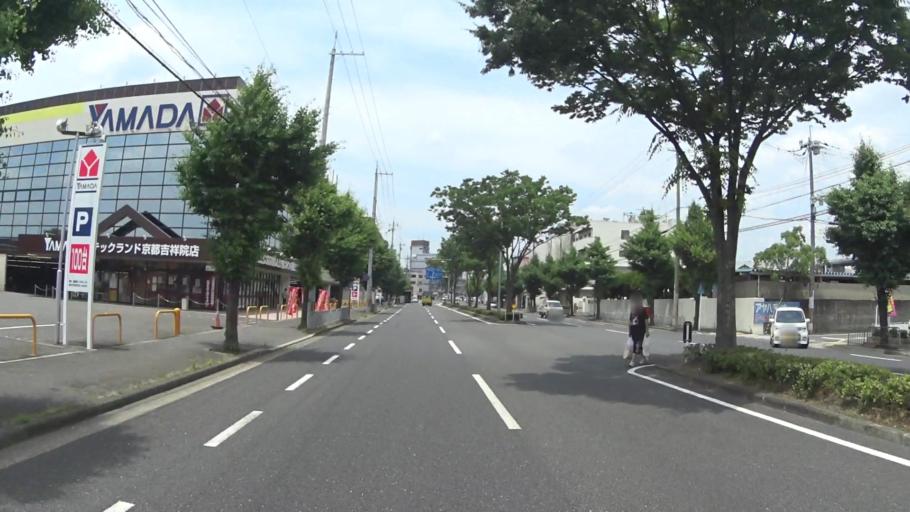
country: JP
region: Kyoto
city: Muko
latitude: 34.9822
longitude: 135.7213
